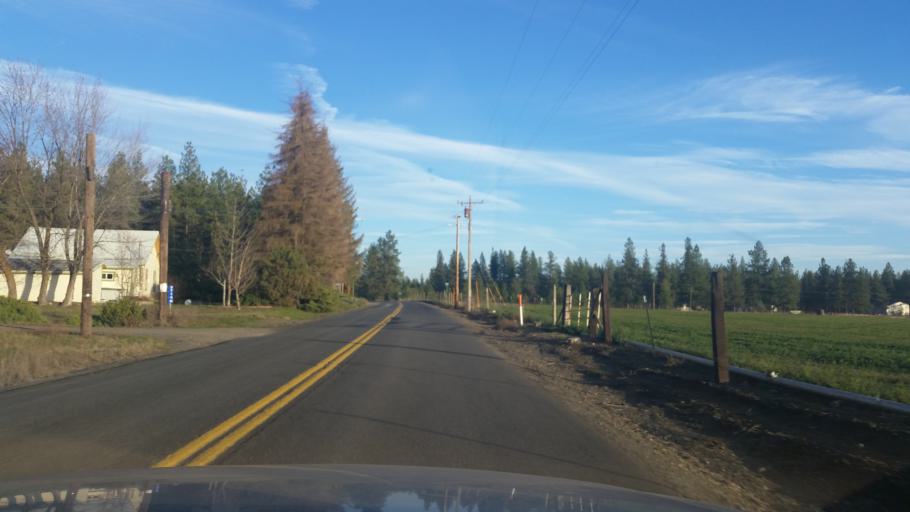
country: US
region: Washington
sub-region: Spokane County
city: Cheney
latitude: 47.5152
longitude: -117.4670
